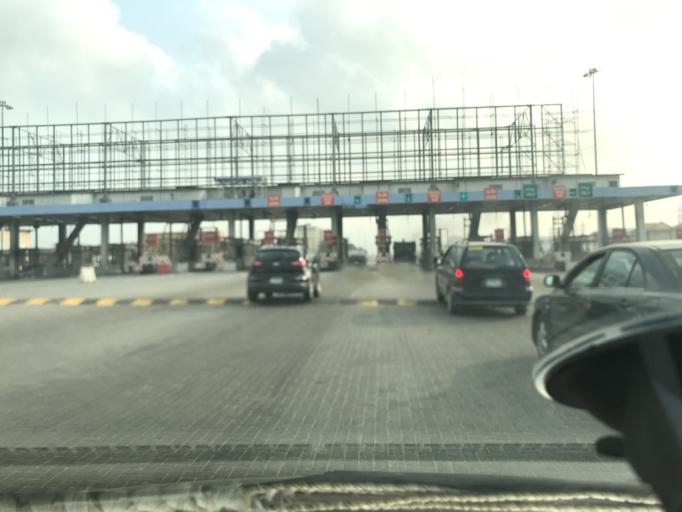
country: NG
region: Lagos
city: Ikoyi
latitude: 6.4447
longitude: 3.5390
